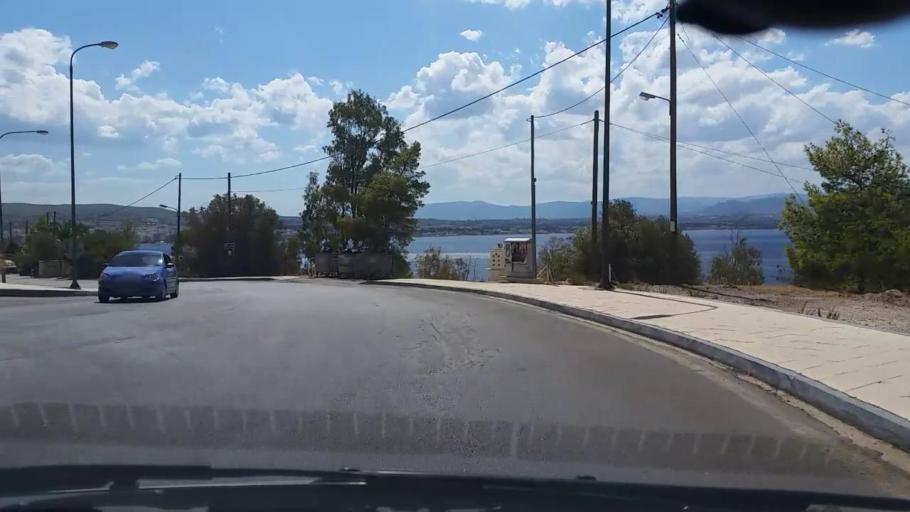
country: GR
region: Peloponnese
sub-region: Nomos Korinthias
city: Loutraki
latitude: 37.9866
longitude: 22.9607
